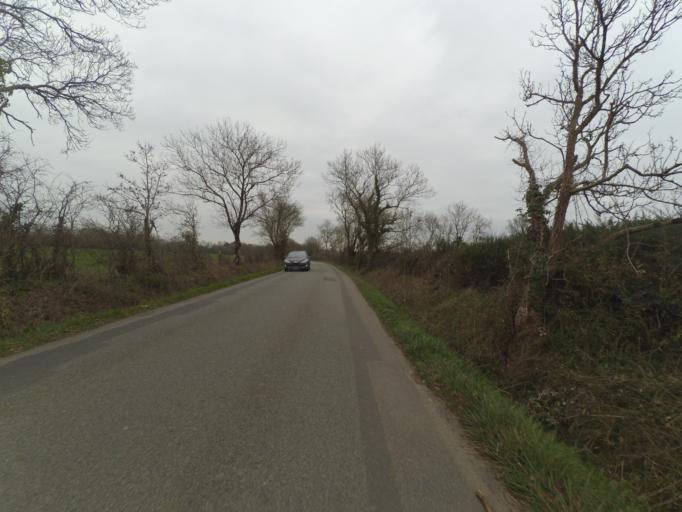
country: FR
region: Pays de la Loire
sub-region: Departement de la Loire-Atlantique
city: Indre
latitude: 47.2291
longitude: -1.6863
